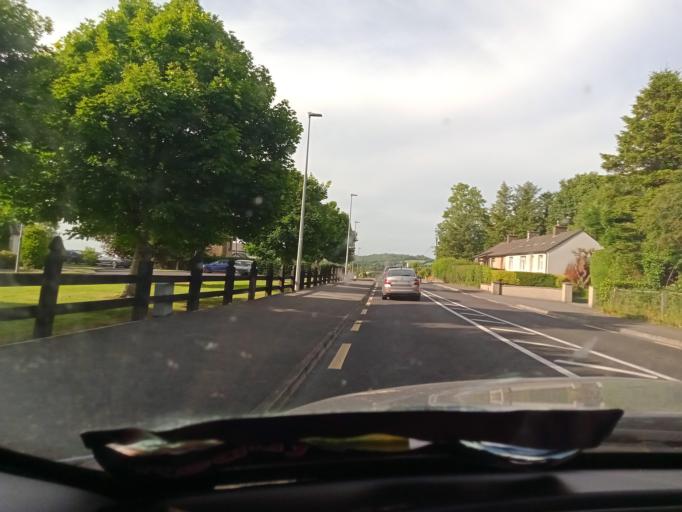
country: IE
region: Ulster
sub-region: An Cabhan
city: Cavan
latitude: 53.9250
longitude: -7.4134
